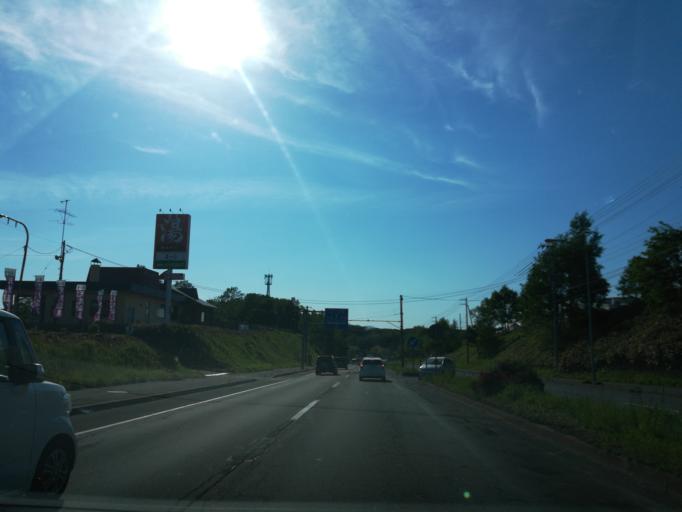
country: JP
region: Hokkaido
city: Kitahiroshima
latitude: 43.0166
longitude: 141.4932
